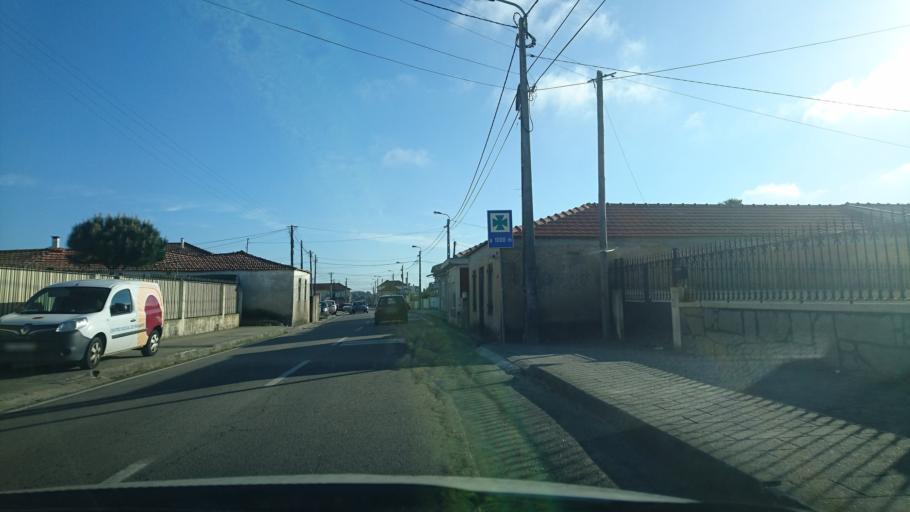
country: PT
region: Aveiro
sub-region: Espinho
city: Souto
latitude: 40.9827
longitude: -8.6321
